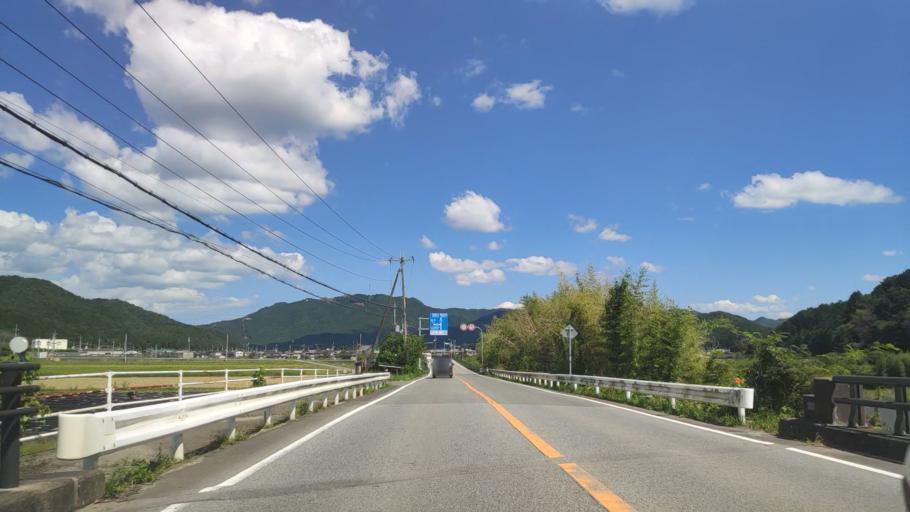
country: JP
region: Kyoto
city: Fukuchiyama
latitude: 35.1928
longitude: 135.1191
